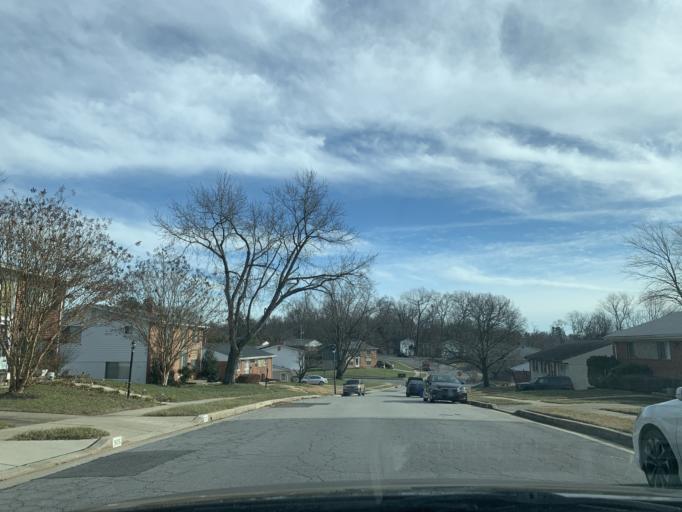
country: US
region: Maryland
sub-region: Baltimore County
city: Pikesville
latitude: 39.3689
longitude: -76.7431
